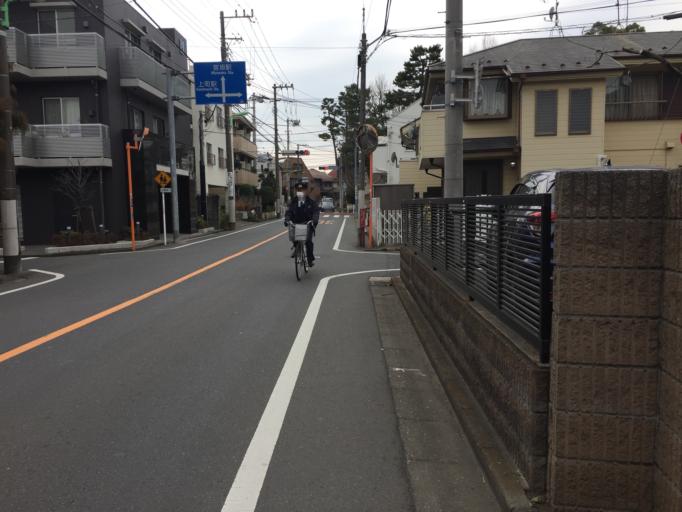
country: JP
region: Tokyo
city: Tokyo
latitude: 35.6456
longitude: 139.6485
